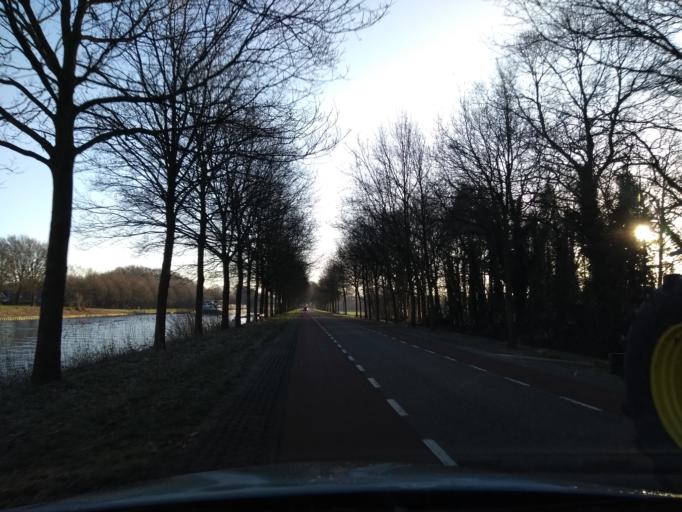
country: NL
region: Overijssel
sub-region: Gemeente Hof van Twente
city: Delden
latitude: 52.2520
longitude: 6.7112
